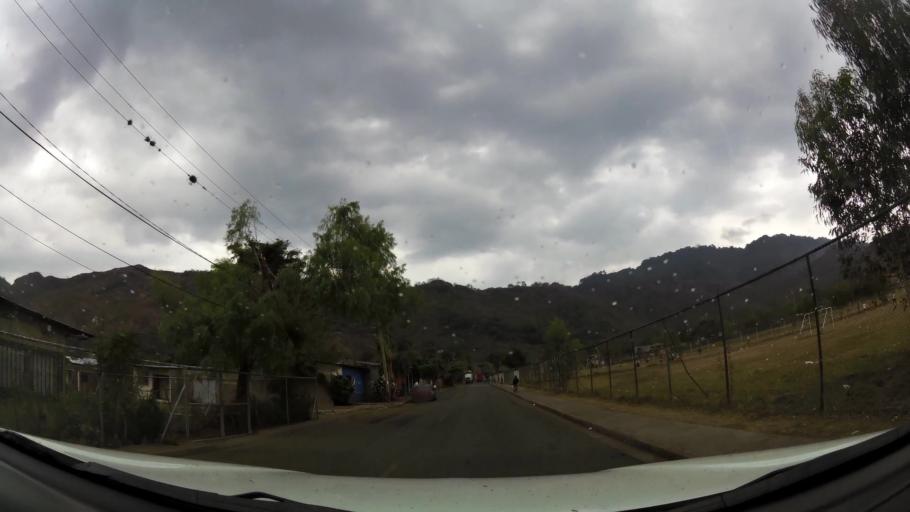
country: NI
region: Jinotega
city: Jinotega
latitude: 13.0897
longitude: -85.9980
